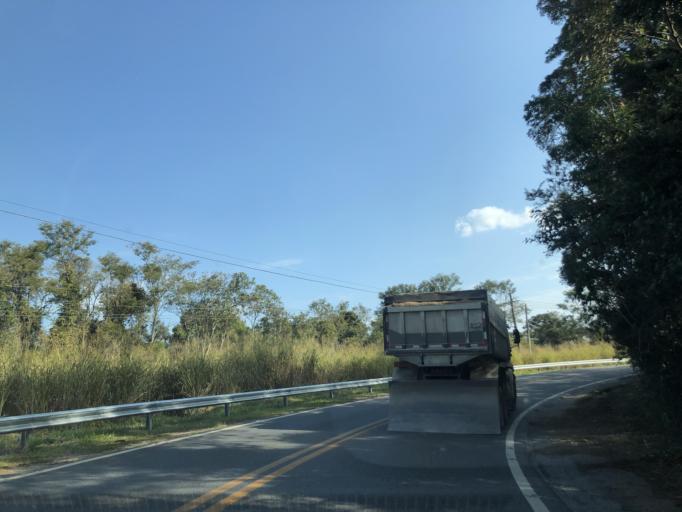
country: BR
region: Sao Paulo
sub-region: Pilar Do Sul
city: Pilar do Sul
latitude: -23.8090
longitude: -47.6949
